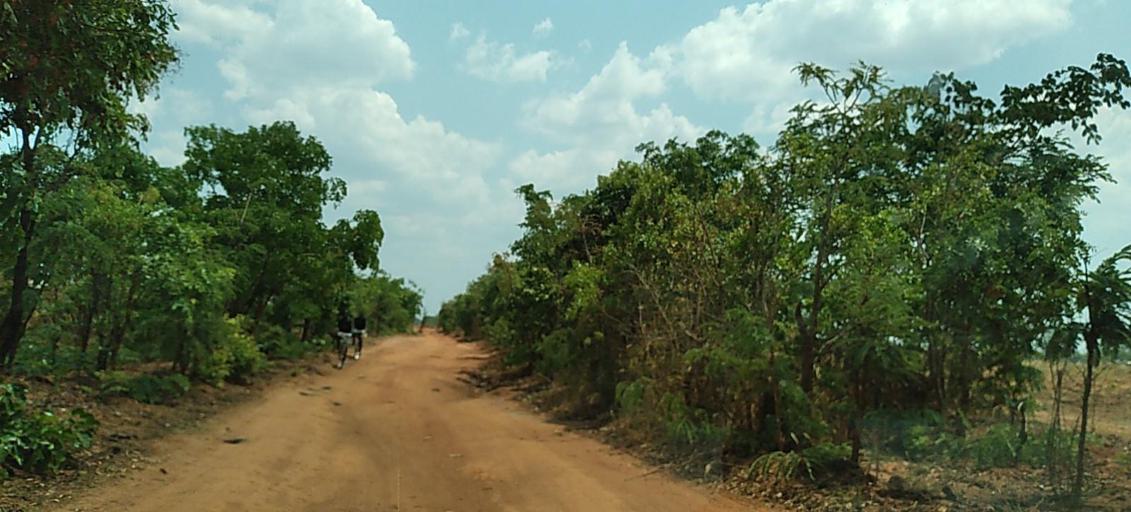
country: ZM
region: Copperbelt
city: Mpongwe
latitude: -13.6586
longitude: 28.0249
